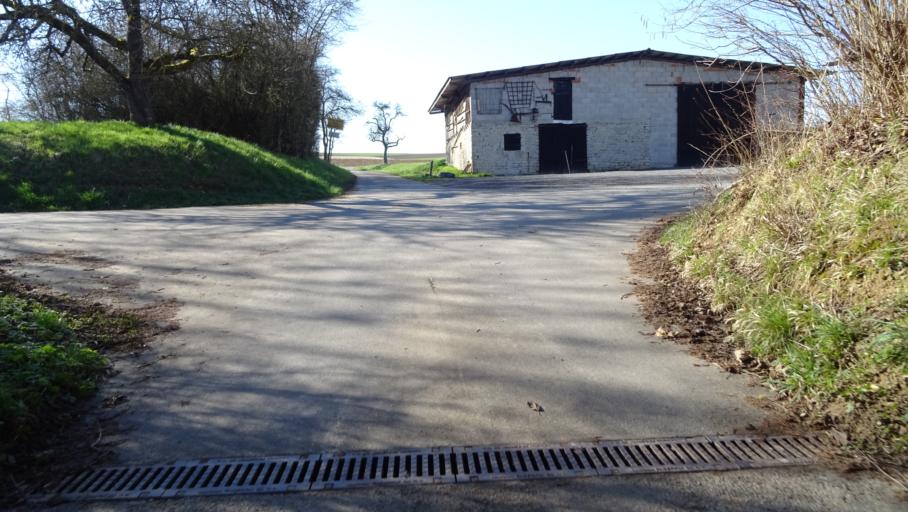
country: DE
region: Baden-Wuerttemberg
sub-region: Karlsruhe Region
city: Seckach
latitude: 49.4281
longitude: 9.2871
